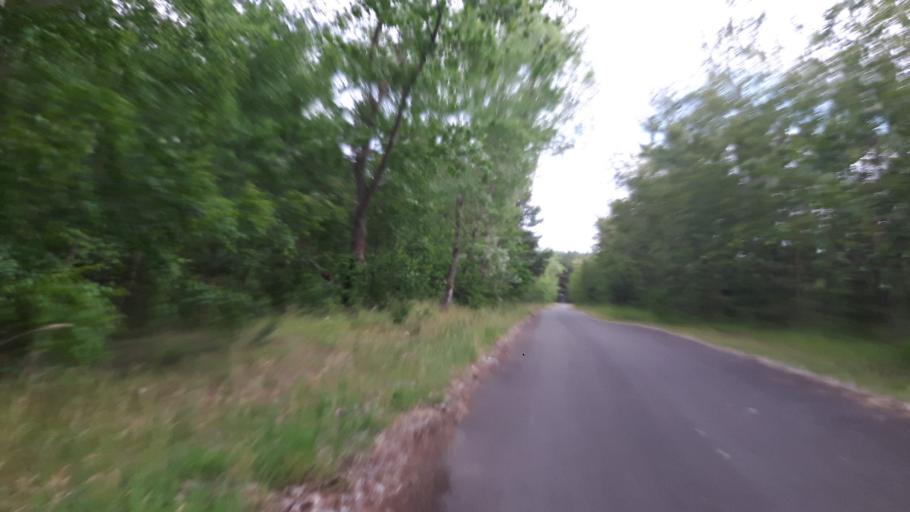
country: DE
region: Saxony-Anhalt
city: Pouch
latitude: 51.5902
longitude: 12.3892
